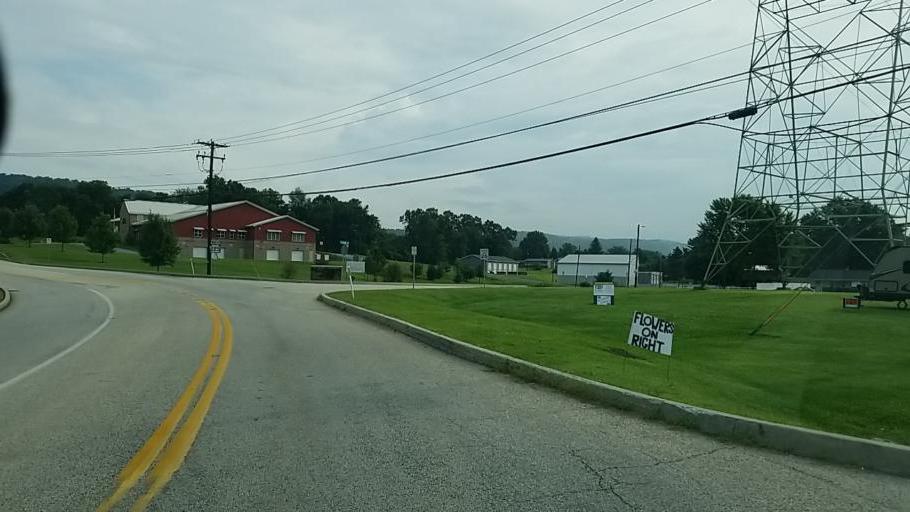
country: US
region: Pennsylvania
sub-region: Perry County
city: Marysville
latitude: 40.3749
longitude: -76.9324
